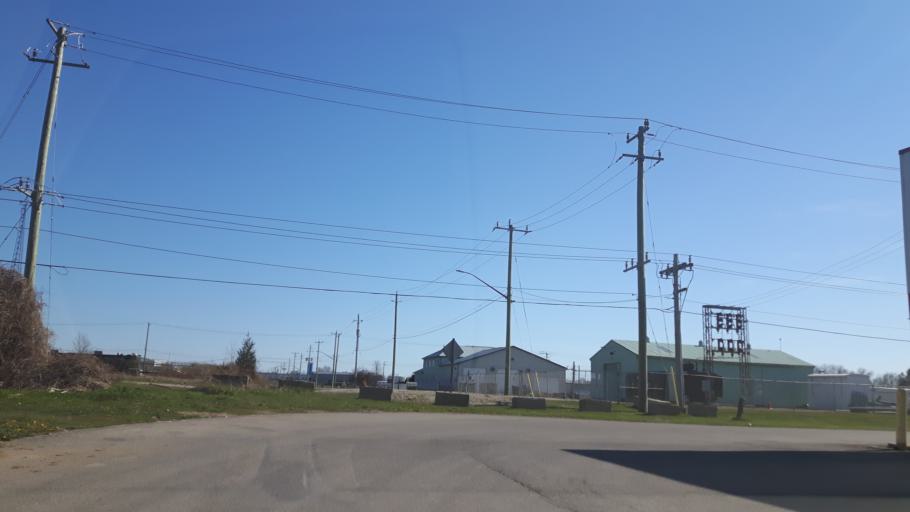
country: CA
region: Ontario
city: Goderich
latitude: 43.7283
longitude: -81.7029
